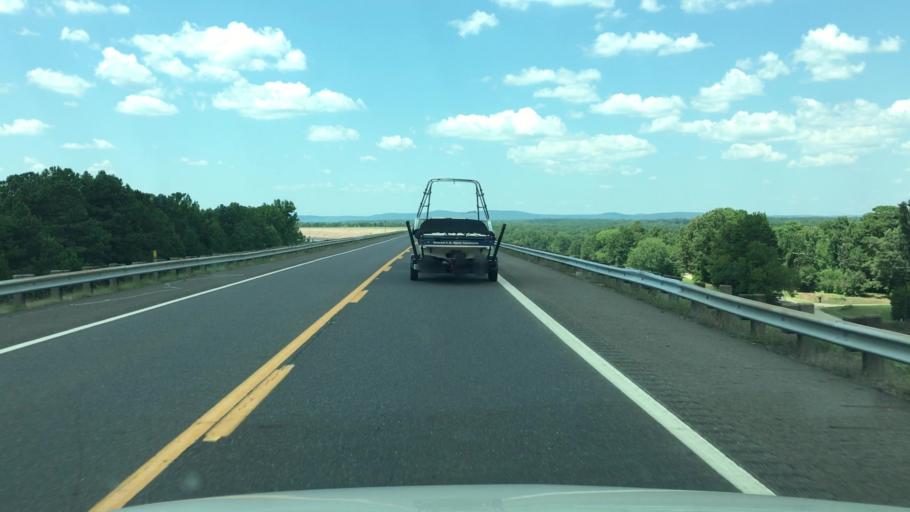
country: US
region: Arkansas
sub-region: Clark County
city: Arkadelphia
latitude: 34.2336
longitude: -93.1006
